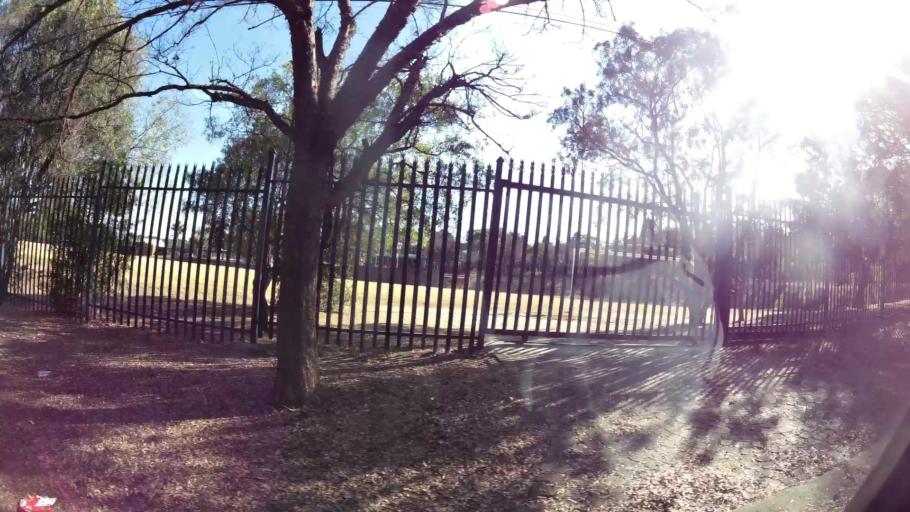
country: ZA
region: Gauteng
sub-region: City of Johannesburg Metropolitan Municipality
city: Roodepoort
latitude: -26.0991
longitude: 27.9566
